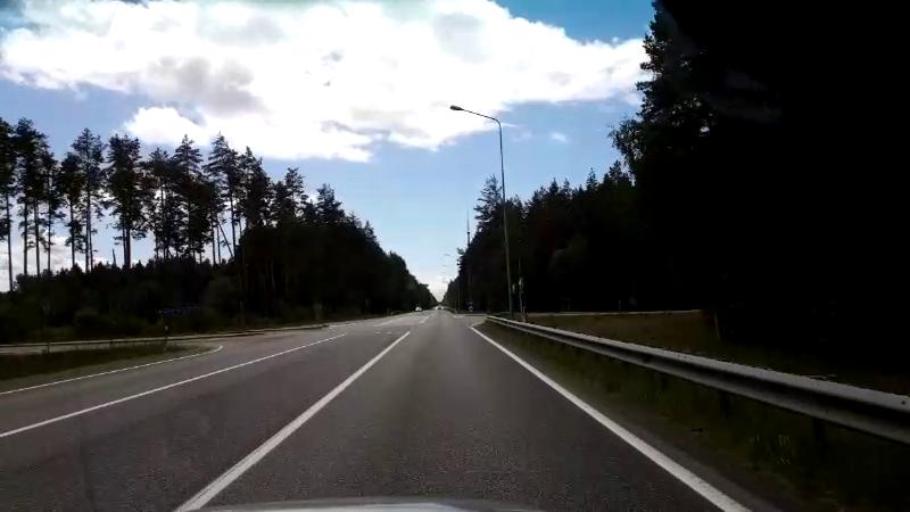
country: LV
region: Saulkrastu
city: Saulkrasti
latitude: 57.4916
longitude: 24.4317
